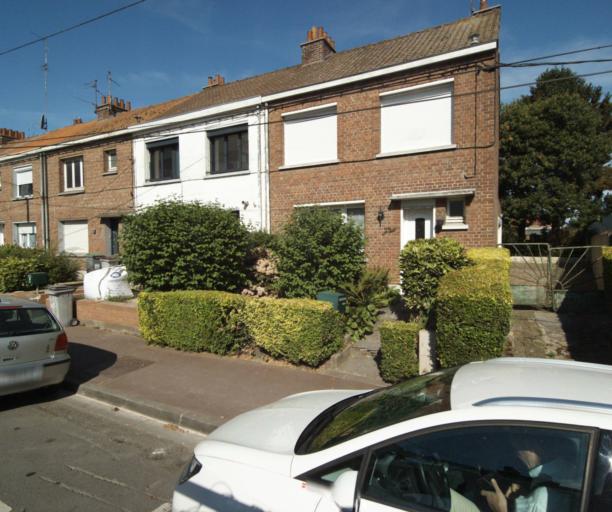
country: FR
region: Nord-Pas-de-Calais
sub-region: Departement du Nord
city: Marcq-en-Baroeul
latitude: 50.6735
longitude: 3.0836
